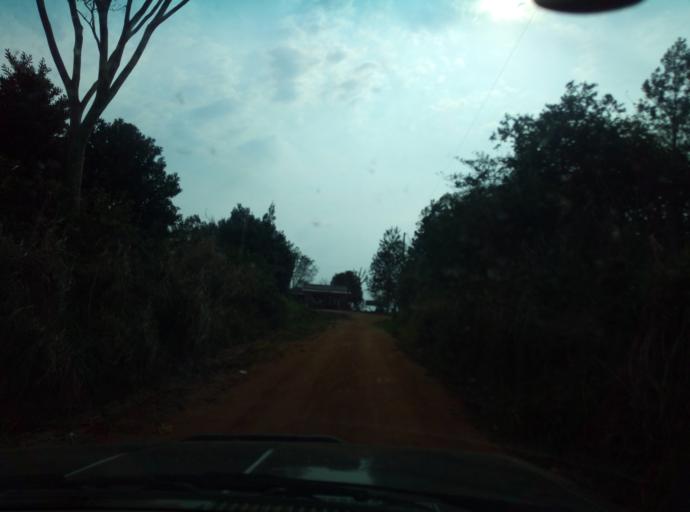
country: PY
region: Caaguazu
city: San Joaquin
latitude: -25.1470
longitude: -56.0984
